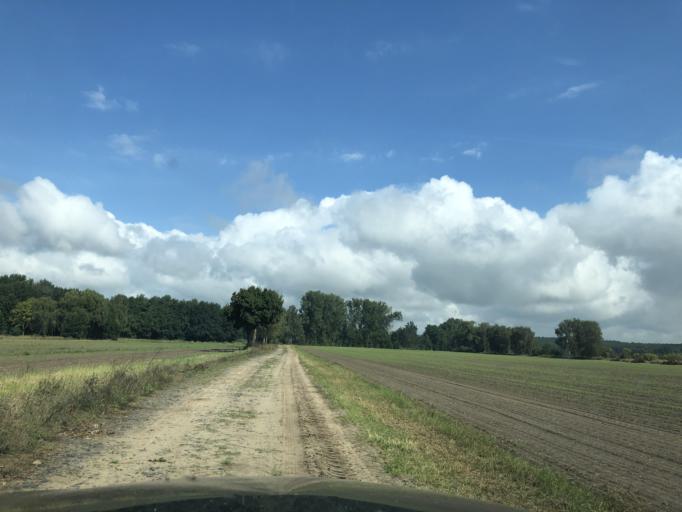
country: DE
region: Brandenburg
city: Schlepzig
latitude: 52.0128
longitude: 13.9595
